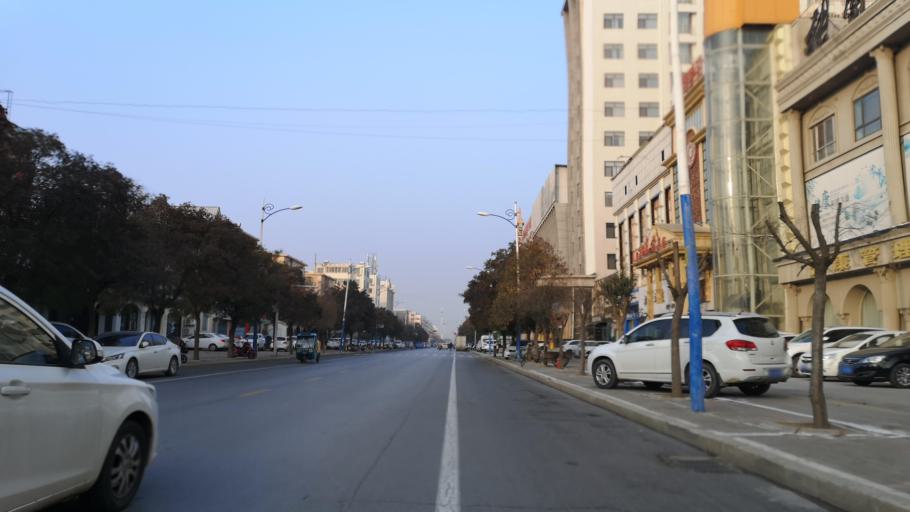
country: CN
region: Henan Sheng
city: Zhongyuanlu
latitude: 35.7672
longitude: 115.0633
